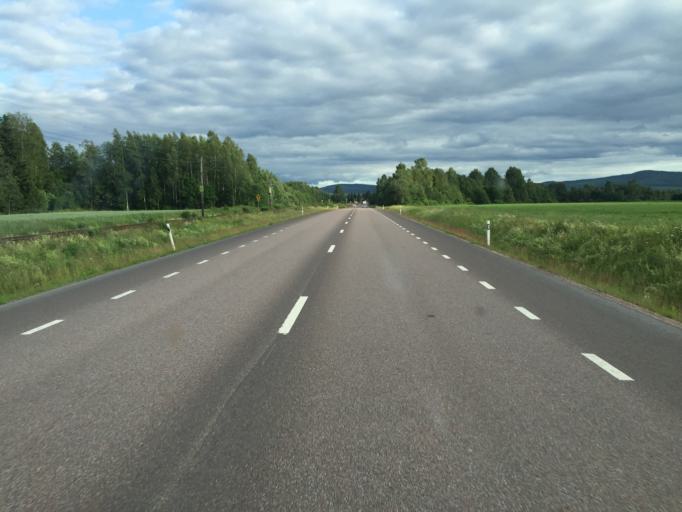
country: SE
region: Dalarna
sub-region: Gagnefs Kommun
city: Djuras
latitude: 60.5718
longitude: 15.1246
